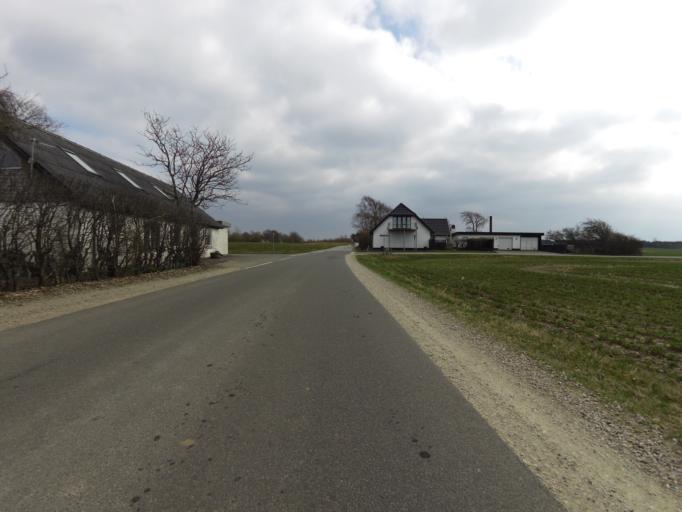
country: DK
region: Central Jutland
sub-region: Holstebro Kommune
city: Holstebro
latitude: 56.4311
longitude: 8.6832
